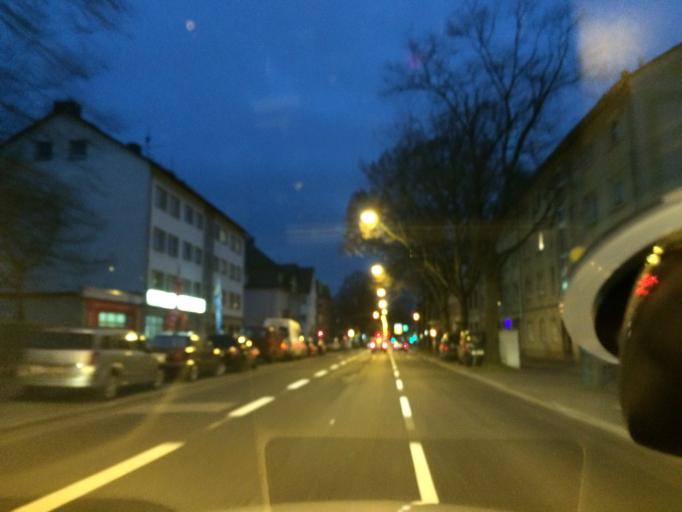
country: DE
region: Hesse
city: Sulzbach
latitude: 50.1122
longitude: 8.5368
